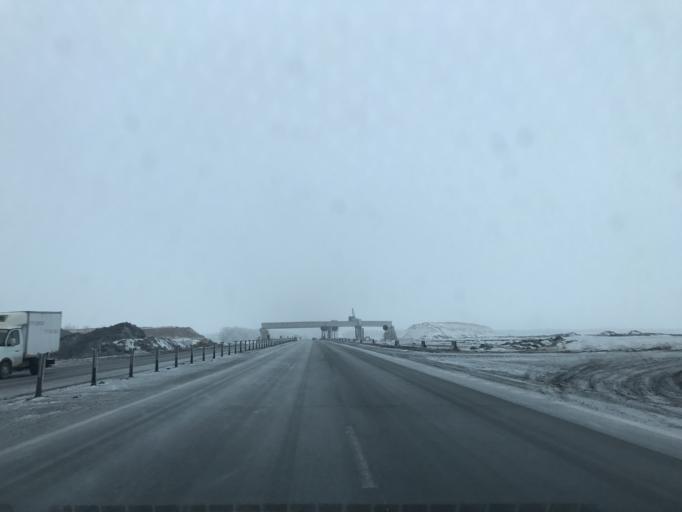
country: RU
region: Rostov
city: Grushevskaya
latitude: 47.5004
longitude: 39.9708
